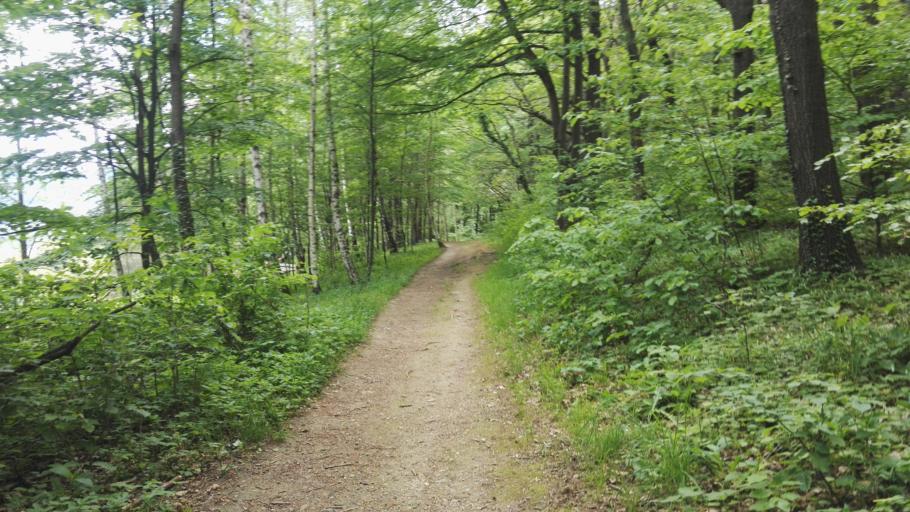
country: AT
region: Styria
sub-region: Graz Stadt
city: Goesting
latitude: 47.0858
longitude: 15.3946
